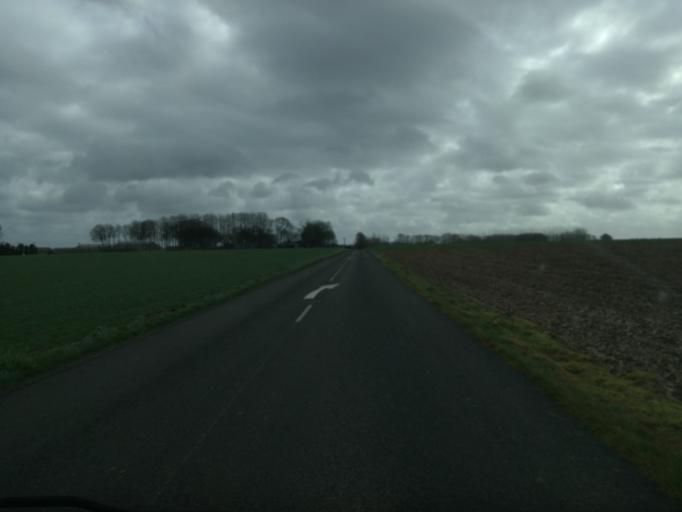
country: FR
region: Haute-Normandie
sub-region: Departement de la Seine-Maritime
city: Yebleron
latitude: 49.6595
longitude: 0.5157
